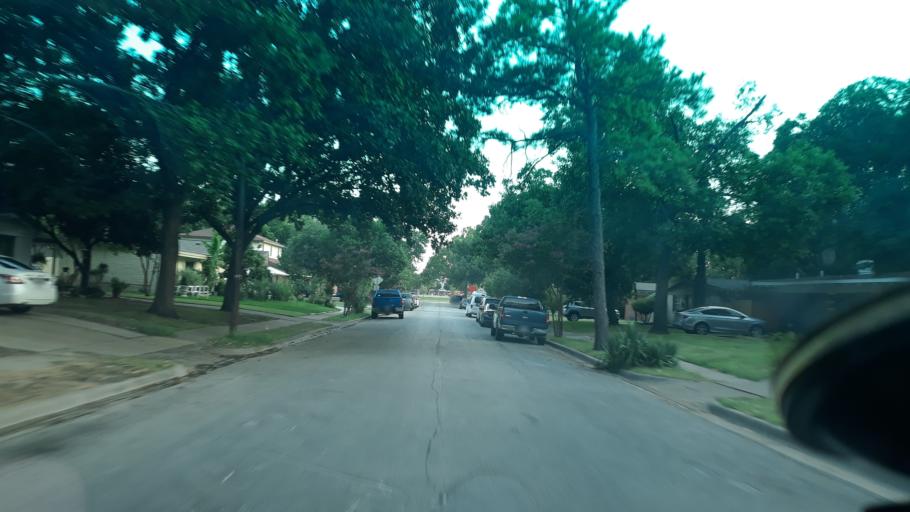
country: US
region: Texas
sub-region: Dallas County
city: Irving
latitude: 32.8329
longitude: -96.9826
